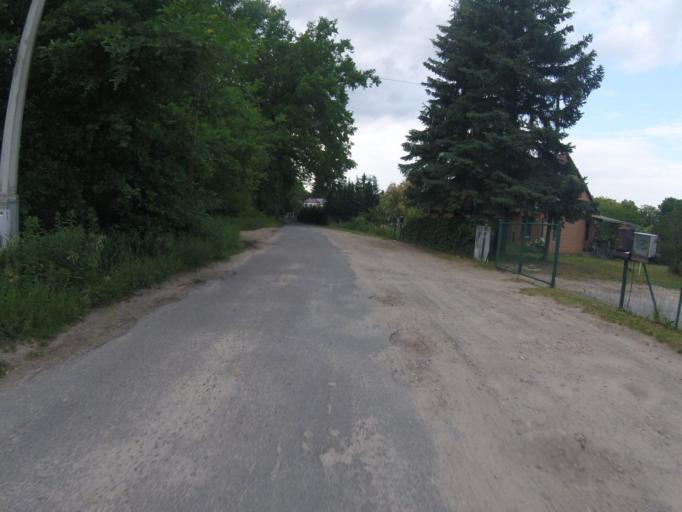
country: DE
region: Brandenburg
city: Konigs Wusterhausen
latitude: 52.2753
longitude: 13.5974
